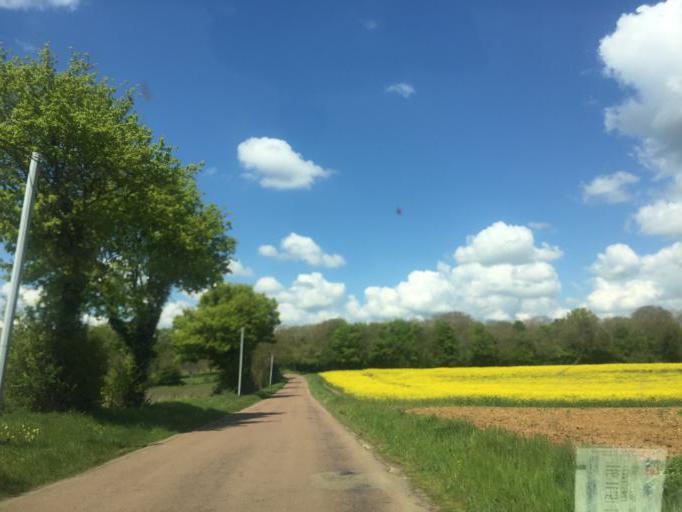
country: FR
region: Bourgogne
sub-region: Departement de l'Yonne
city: Fontenailles
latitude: 47.4962
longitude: 3.3700
